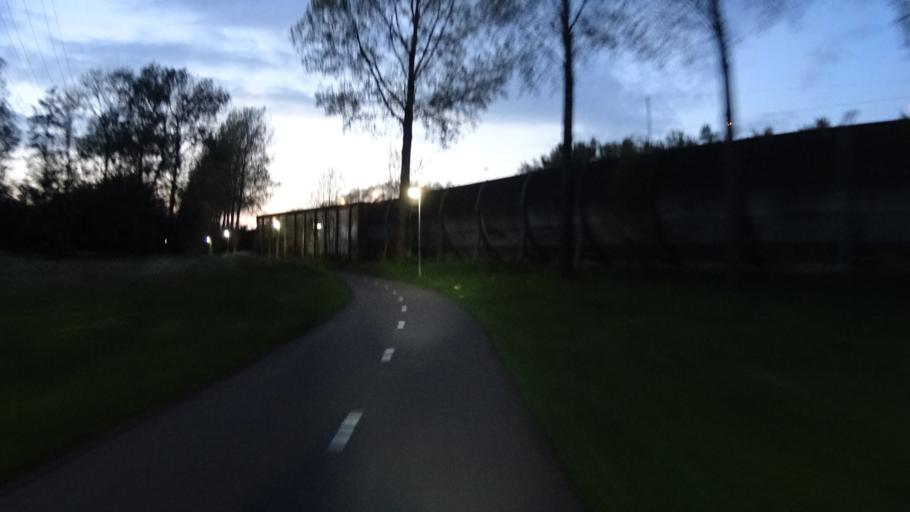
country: NL
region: South Holland
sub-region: Gemeente Papendrecht
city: Papendrecht
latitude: 51.8427
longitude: 4.6968
